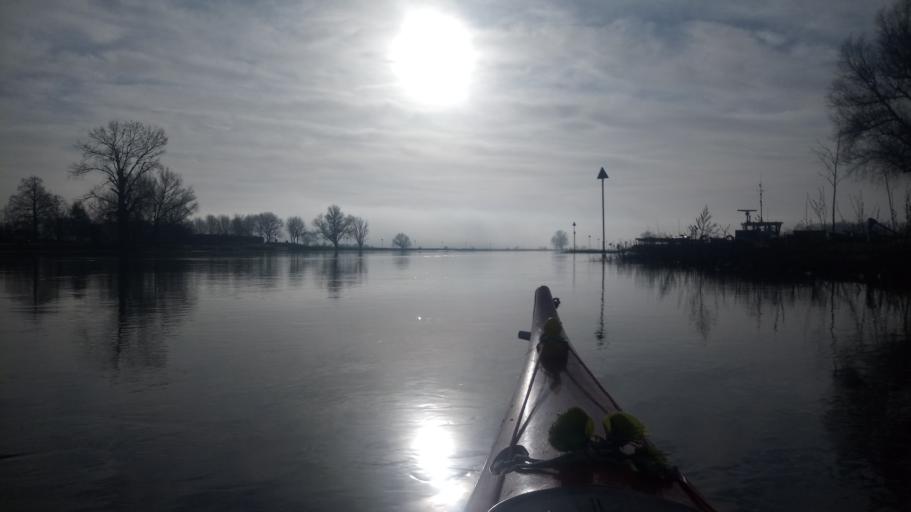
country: NL
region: Gelderland
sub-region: Gemeente Brummen
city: Brummen
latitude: 52.0831
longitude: 6.1715
